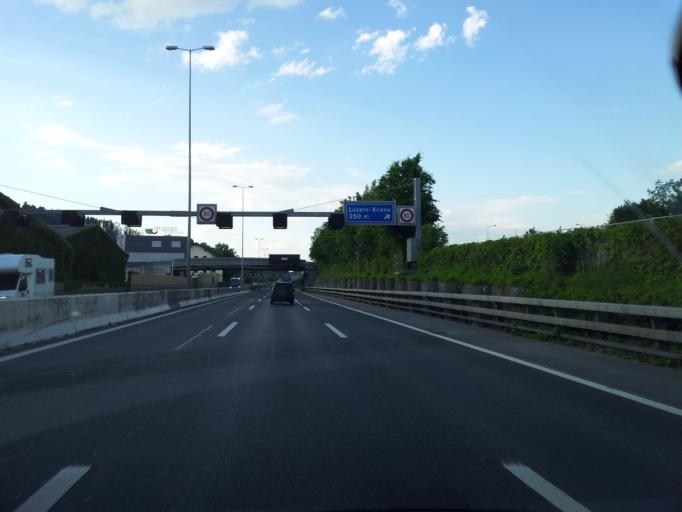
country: CH
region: Lucerne
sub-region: Lucerne-Land District
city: Kriens
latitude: 47.0305
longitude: 8.2946
